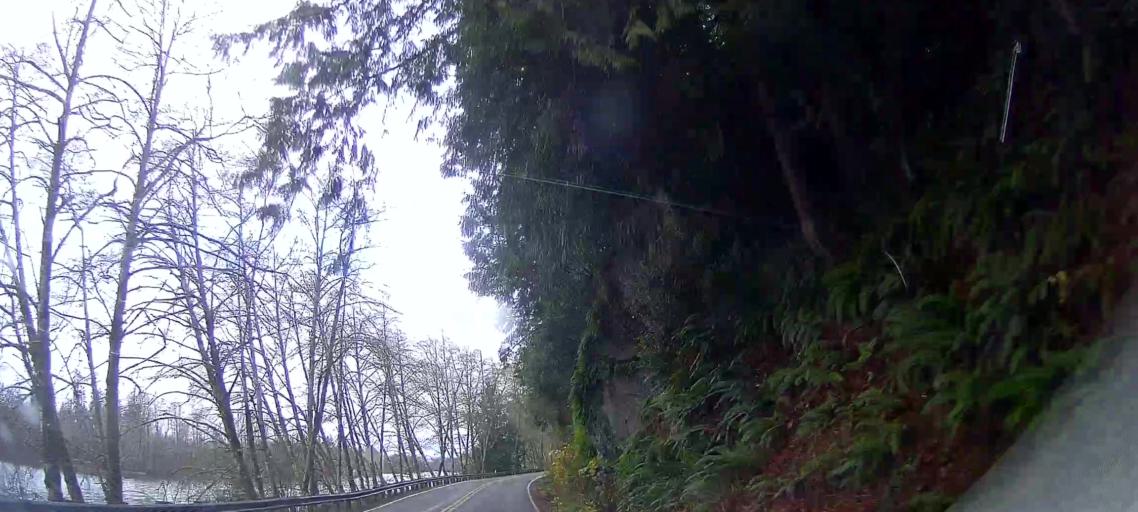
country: US
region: Washington
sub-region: Skagit County
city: Sedro-Woolley
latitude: 48.5145
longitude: -121.9857
